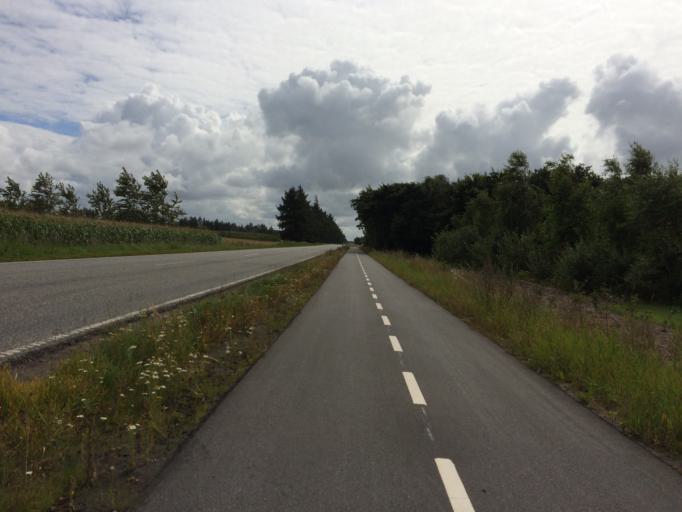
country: DK
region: Central Jutland
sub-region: Holstebro Kommune
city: Ulfborg
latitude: 56.3085
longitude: 8.3386
